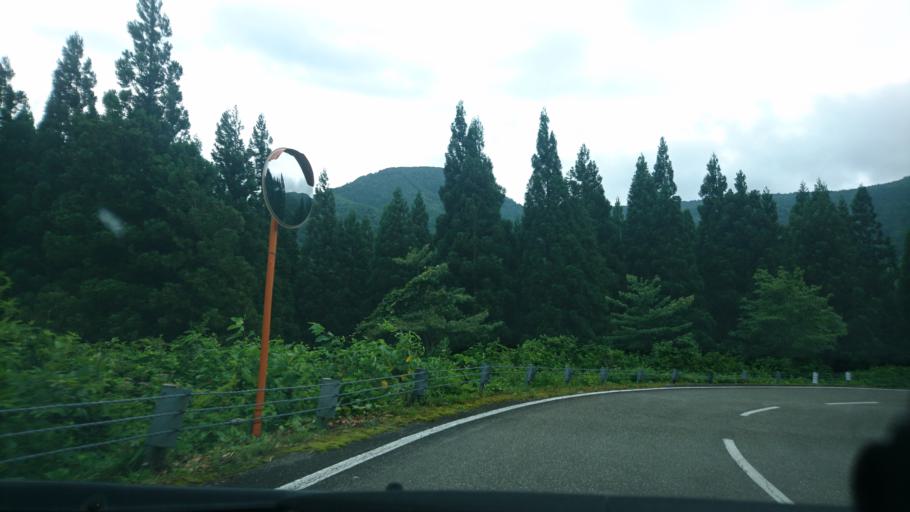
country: JP
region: Akita
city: Yuzawa
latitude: 39.1619
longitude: 140.7461
